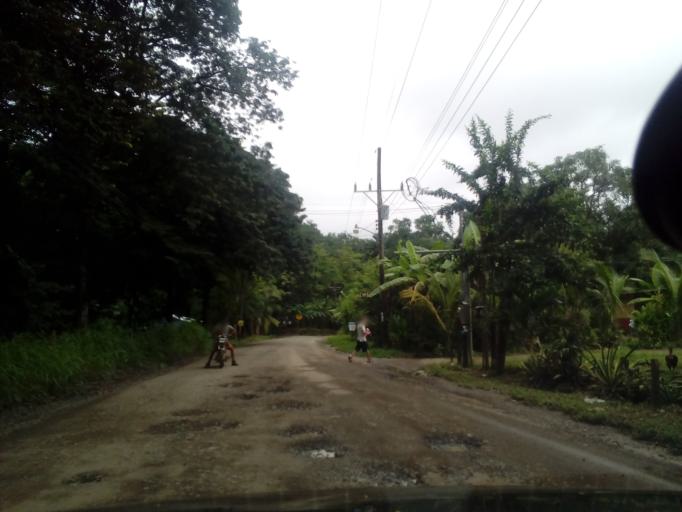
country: CR
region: Guanacaste
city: Samara
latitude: 9.9386
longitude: -85.6495
